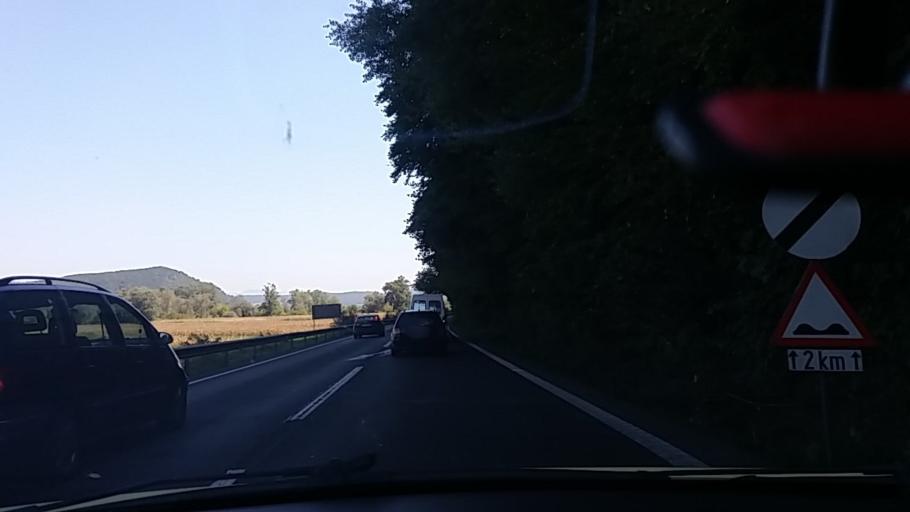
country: RO
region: Hunedoara
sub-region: Comuna Ilia
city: Ilia
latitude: 45.9201
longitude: 22.7074
